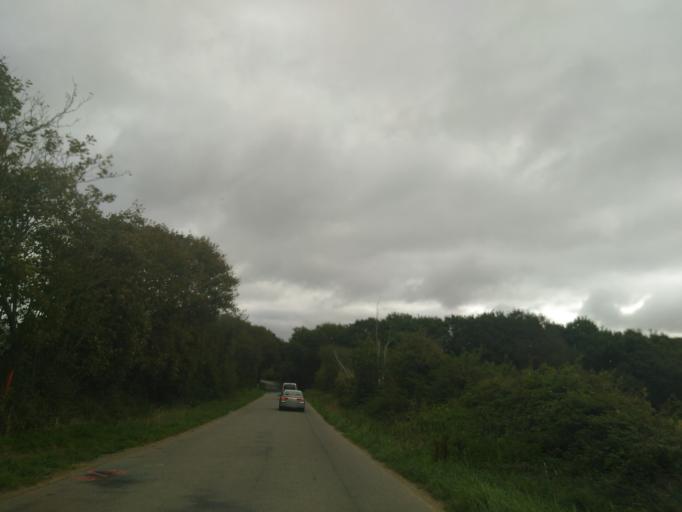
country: FR
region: Brittany
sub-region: Departement du Finistere
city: Plomodiern
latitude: 48.1602
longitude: -4.2539
